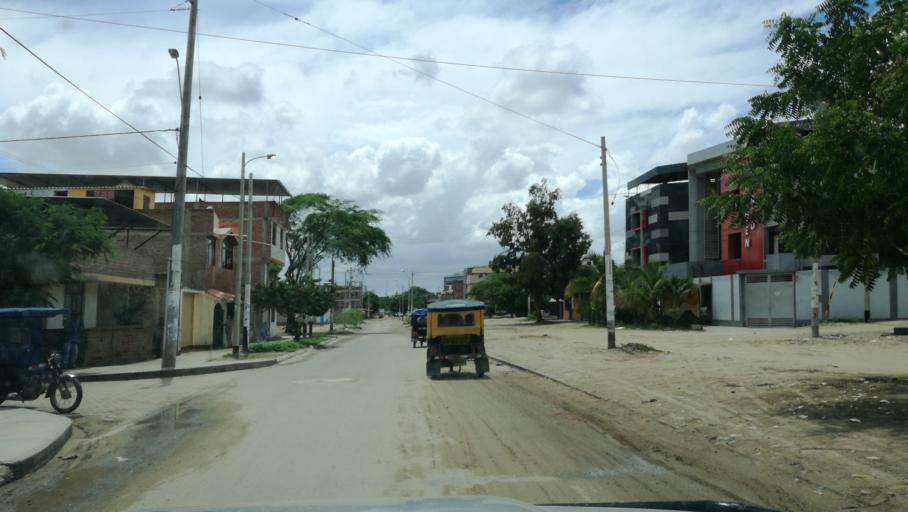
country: PE
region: Piura
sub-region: Provincia de Piura
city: Piura
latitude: -5.1788
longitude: -80.6457
